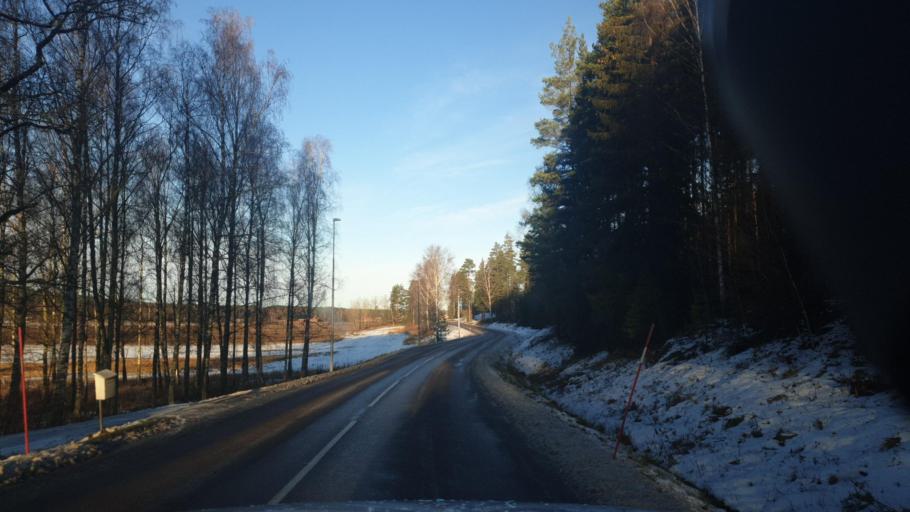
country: SE
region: Vaermland
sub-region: Arvika Kommun
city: Arvika
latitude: 59.5619
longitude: 12.5569
